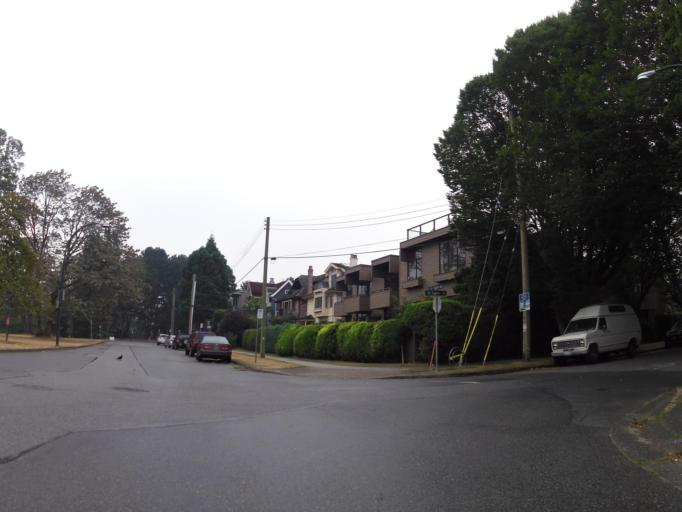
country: CA
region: British Columbia
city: West End
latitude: 49.2768
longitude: -123.1478
